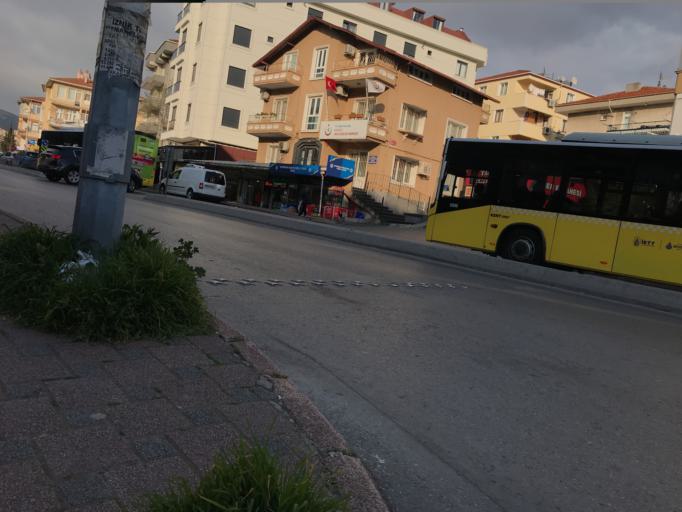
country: TR
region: Istanbul
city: Maltepe
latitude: 40.9305
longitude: 29.1347
